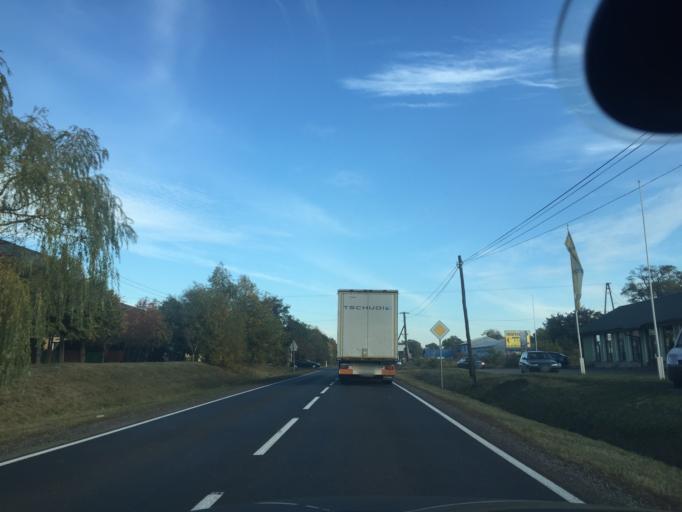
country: PL
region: Kujawsko-Pomorskie
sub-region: Powiat mogilenski
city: Strzelno
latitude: 52.6279
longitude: 18.1575
